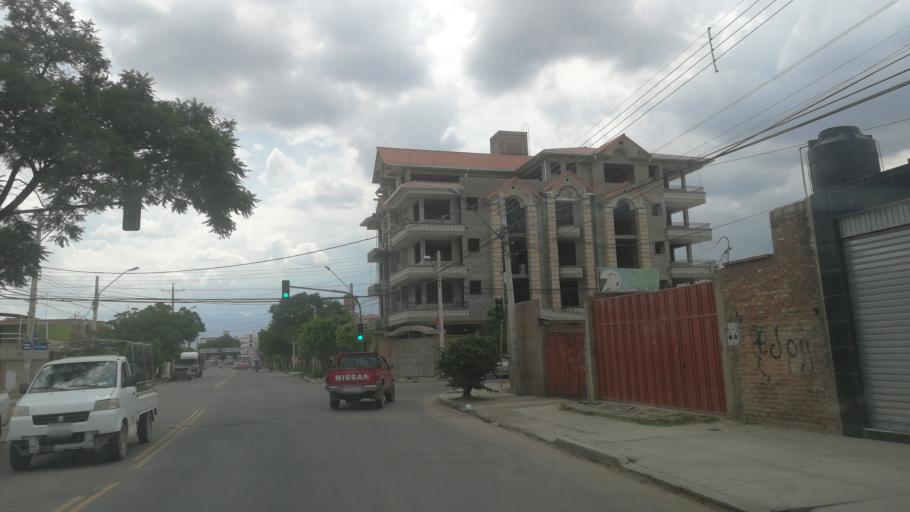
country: BO
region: Cochabamba
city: Cochabamba
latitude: -17.4019
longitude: -66.1805
